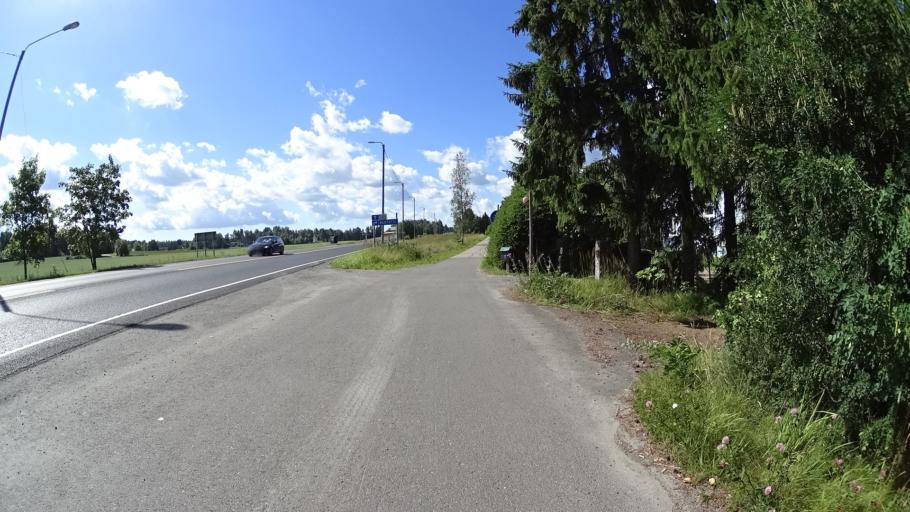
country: FI
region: Uusimaa
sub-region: Helsinki
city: Jaervenpaeae
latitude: 60.4448
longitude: 25.0769
